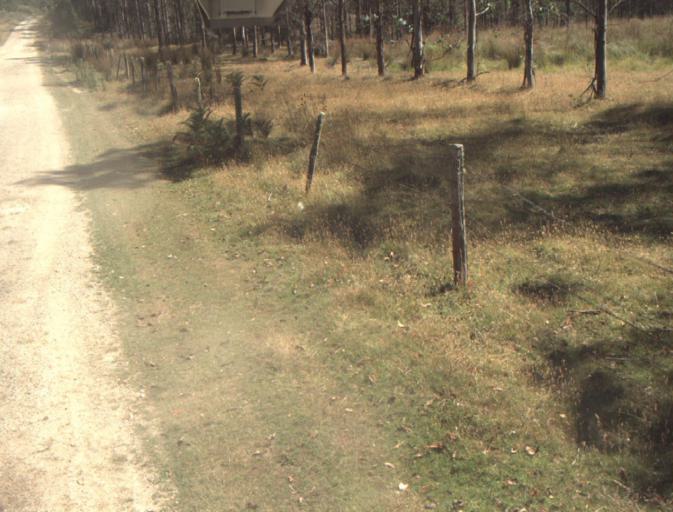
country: AU
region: Tasmania
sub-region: Dorset
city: Scottsdale
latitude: -41.2605
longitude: 147.3495
